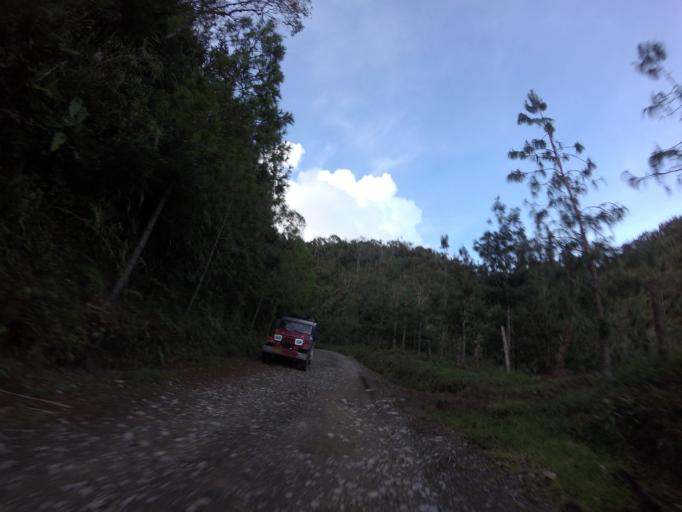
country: CO
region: Caldas
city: Pensilvania
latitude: 5.4585
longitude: -75.1217
